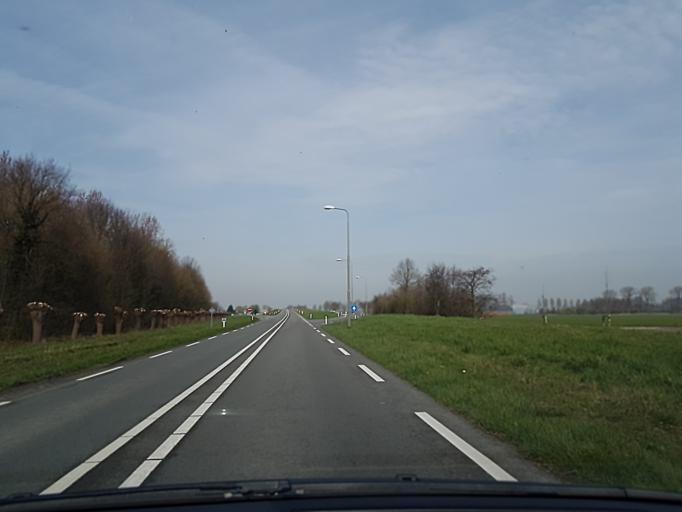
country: NL
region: Zeeland
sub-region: Gemeente Hulst
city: Hulst
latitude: 51.3704
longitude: 4.0233
